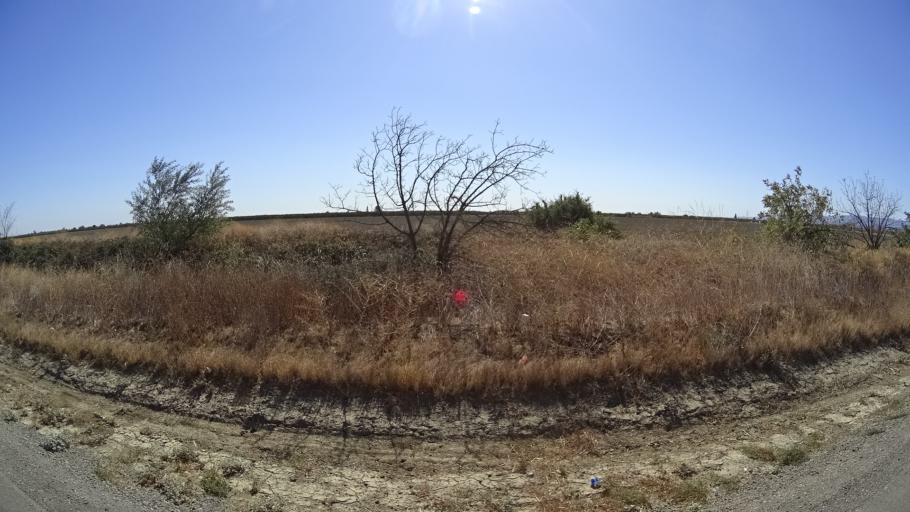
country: US
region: California
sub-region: Yolo County
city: Winters
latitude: 38.5615
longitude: -121.8969
